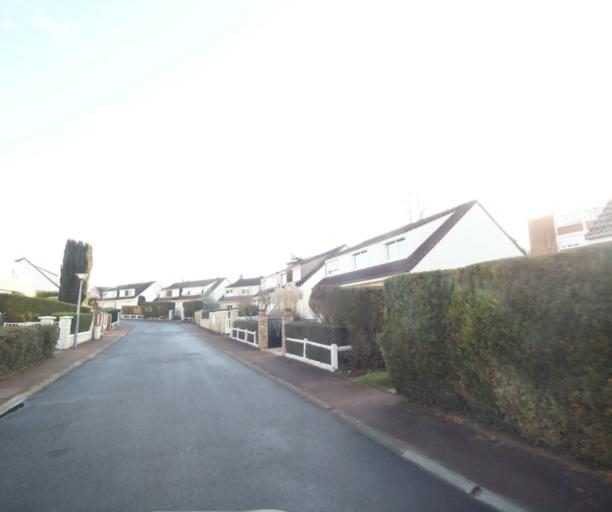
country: FR
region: Ile-de-France
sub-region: Departement des Yvelines
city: Meulan-en-Yvelines
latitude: 49.0108
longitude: 1.9172
